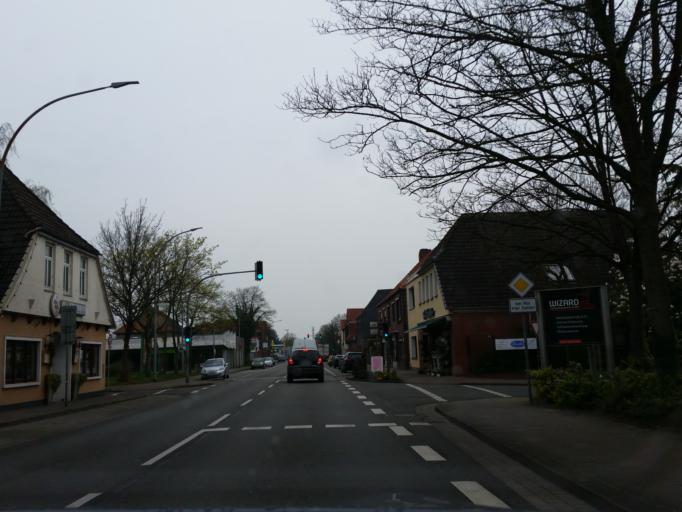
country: DE
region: Lower Saxony
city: Bremervorde
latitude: 53.4885
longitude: 9.1413
